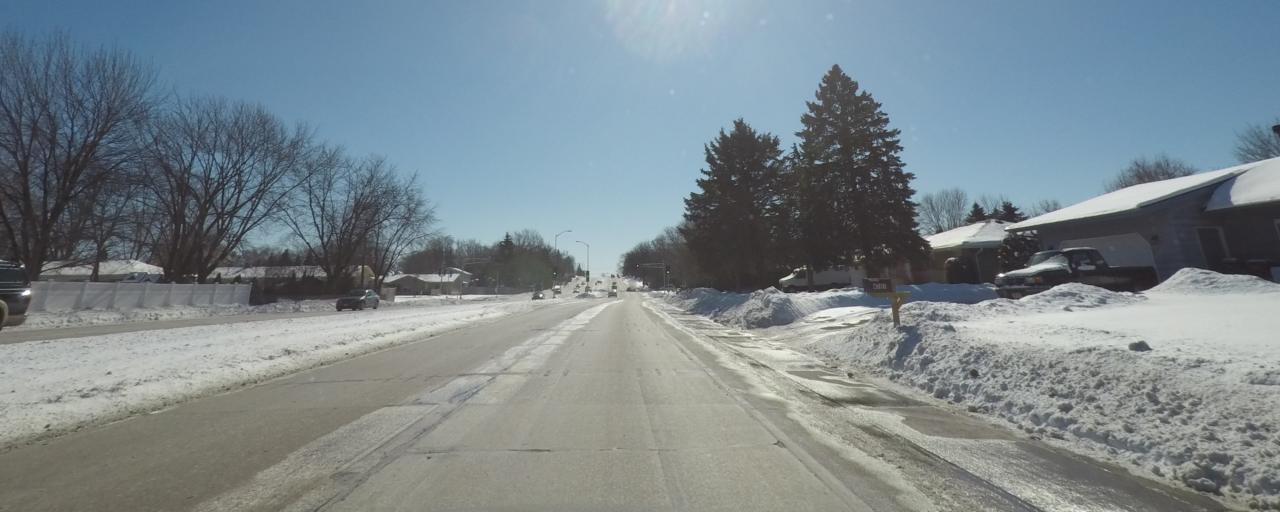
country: US
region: Wisconsin
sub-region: Waukesha County
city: New Berlin
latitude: 42.9682
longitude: -88.1088
